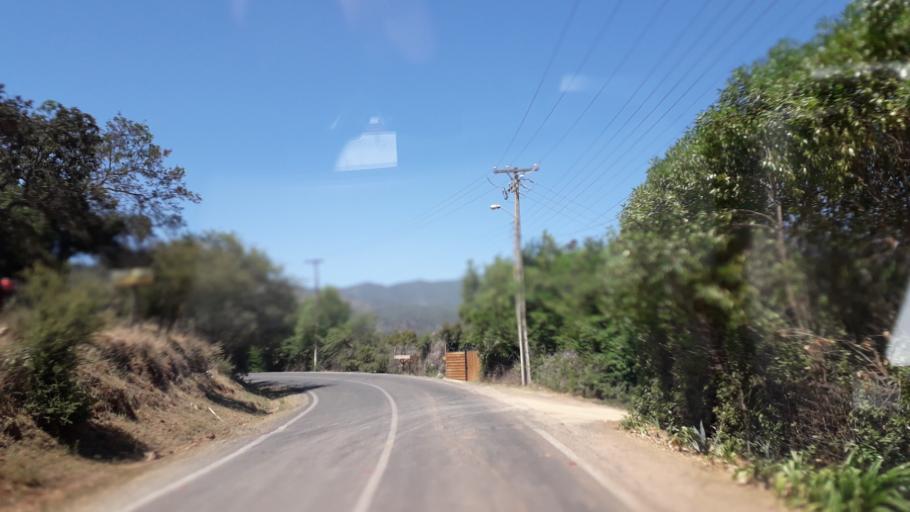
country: CL
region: Valparaiso
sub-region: Provincia de Marga Marga
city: Limache
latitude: -33.0843
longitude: -71.2124
